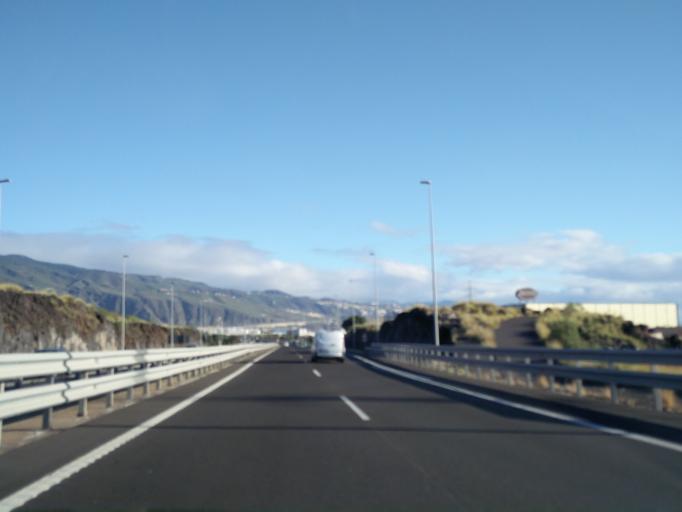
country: ES
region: Canary Islands
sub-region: Provincia de Santa Cruz de Tenerife
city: Candelaria
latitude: 28.3269
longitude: -16.3765
